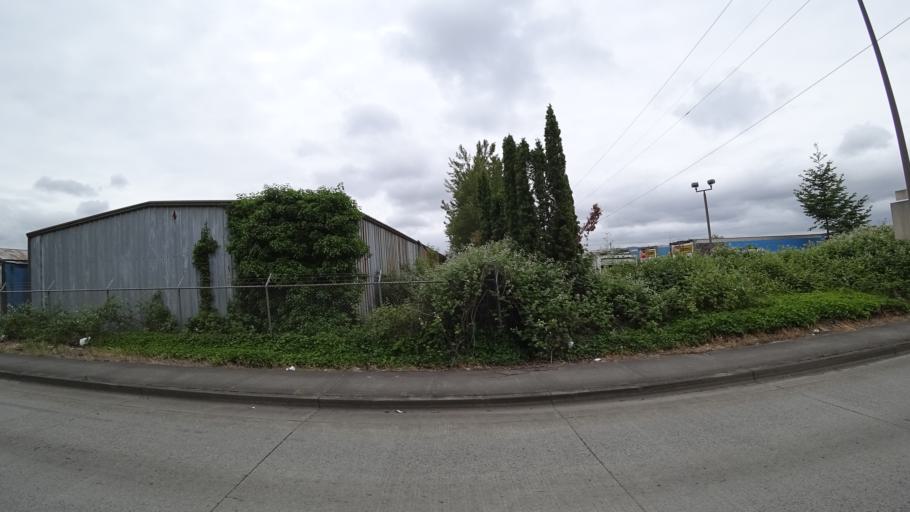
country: US
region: Washington
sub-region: Clark County
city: Vancouver
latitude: 45.6147
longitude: -122.7071
